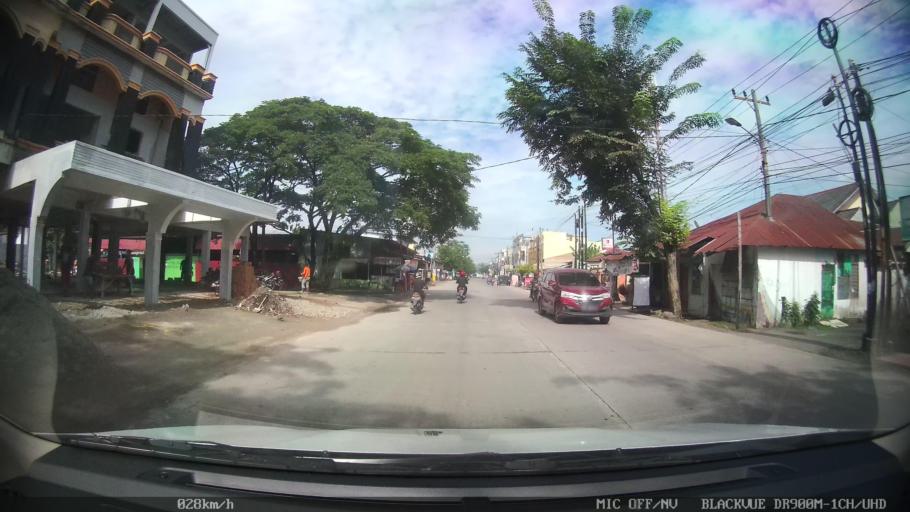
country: ID
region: North Sumatra
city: Sunggal
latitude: 3.6054
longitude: 98.6248
